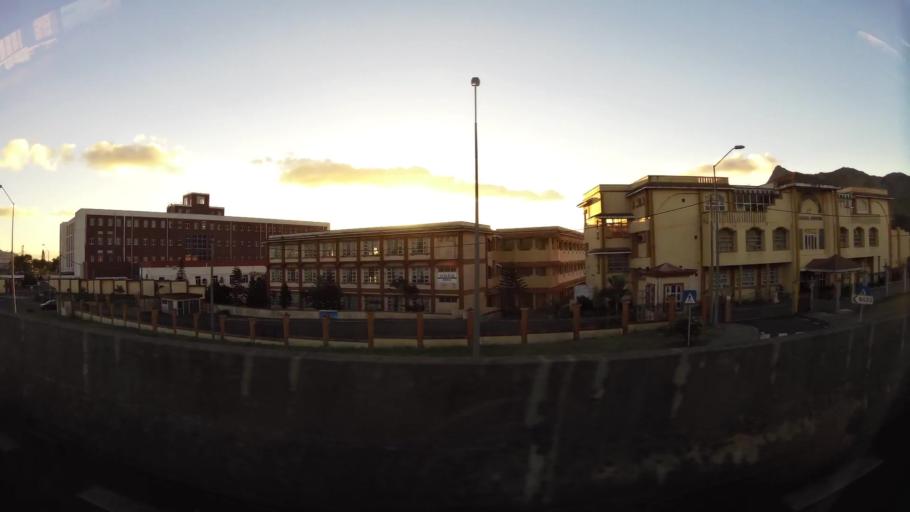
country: MU
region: Moka
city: Moka
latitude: -20.2295
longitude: 57.5034
